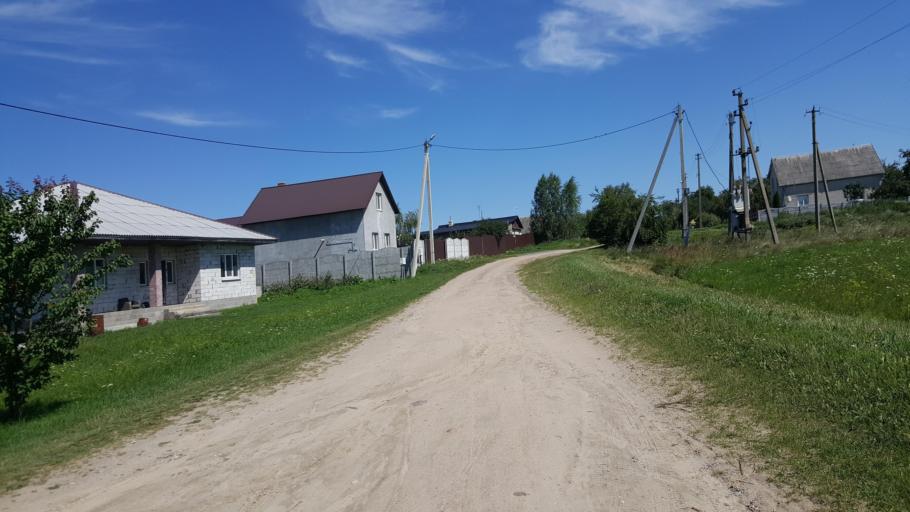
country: BY
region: Brest
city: Charnawchytsy
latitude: 52.2216
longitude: 23.7324
